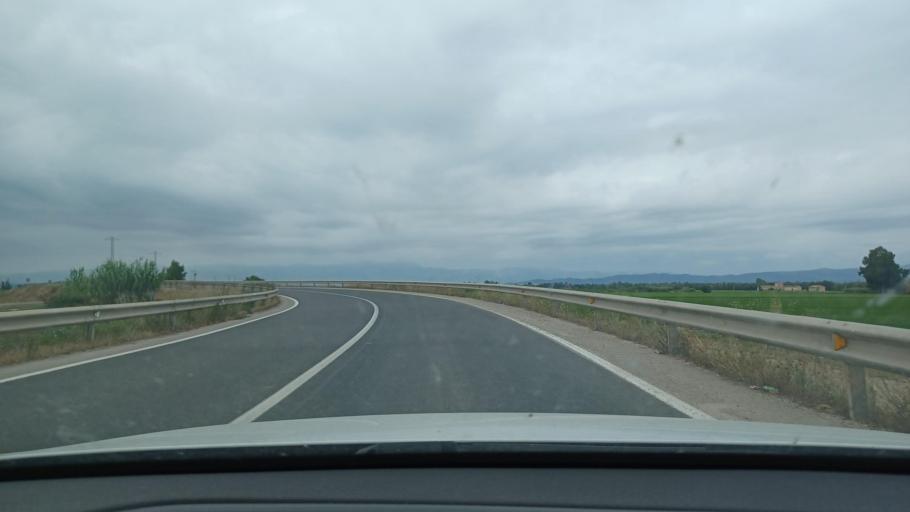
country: ES
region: Catalonia
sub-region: Provincia de Tarragona
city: Deltebre
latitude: 40.7054
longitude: 0.7072
